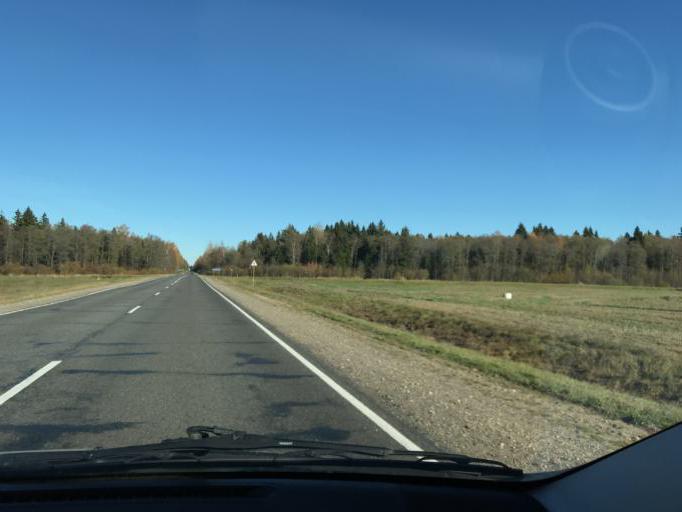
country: BY
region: Vitebsk
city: Lyepyel'
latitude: 54.9408
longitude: 28.7402
